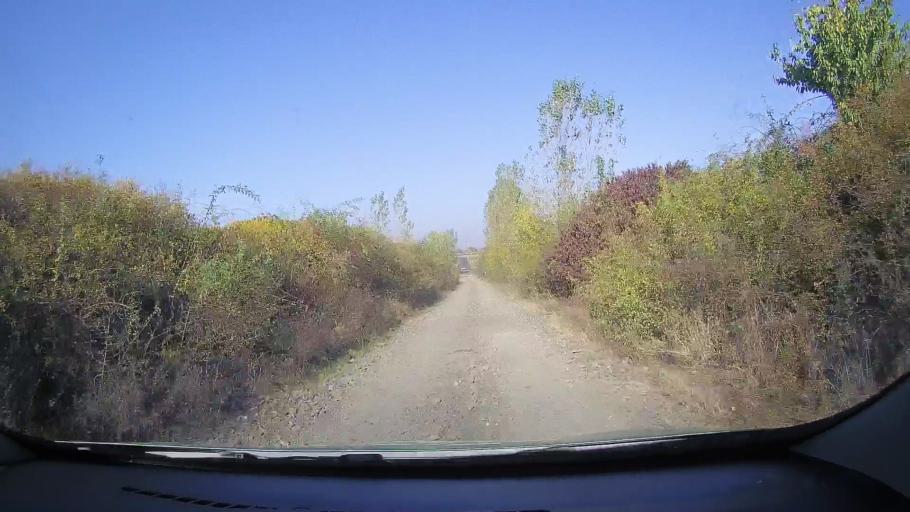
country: RO
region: Satu Mare
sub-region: Comuna Sauca
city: Sauca
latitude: 47.4845
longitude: 22.4626
